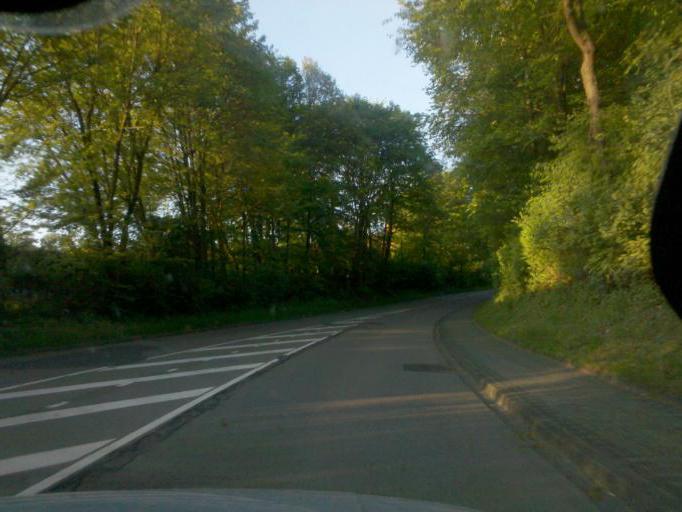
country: DE
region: North Rhine-Westphalia
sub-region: Regierungsbezirk Koln
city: Gummersbach
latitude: 51.0138
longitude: 7.5628
